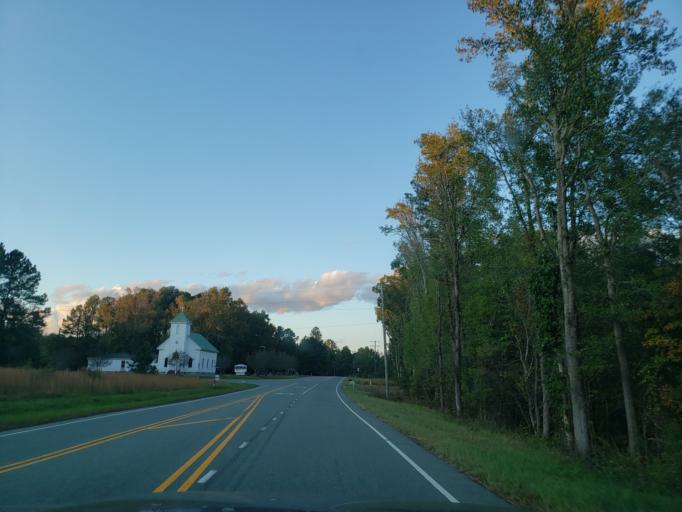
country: US
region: North Carolina
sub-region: Wake County
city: Green Level
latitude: 35.7895
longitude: -78.9638
